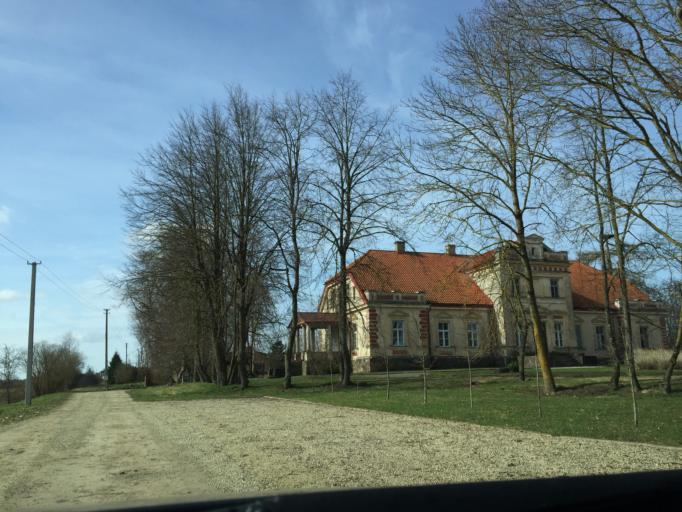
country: LT
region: Siauliu apskritis
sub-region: Joniskis
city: Joniskis
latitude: 56.1805
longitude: 23.5320
